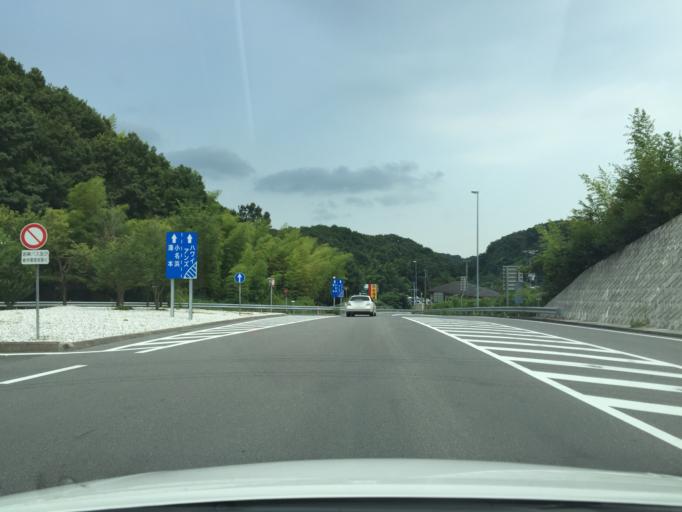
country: JP
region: Fukushima
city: Iwaki
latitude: 37.0016
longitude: 140.8136
